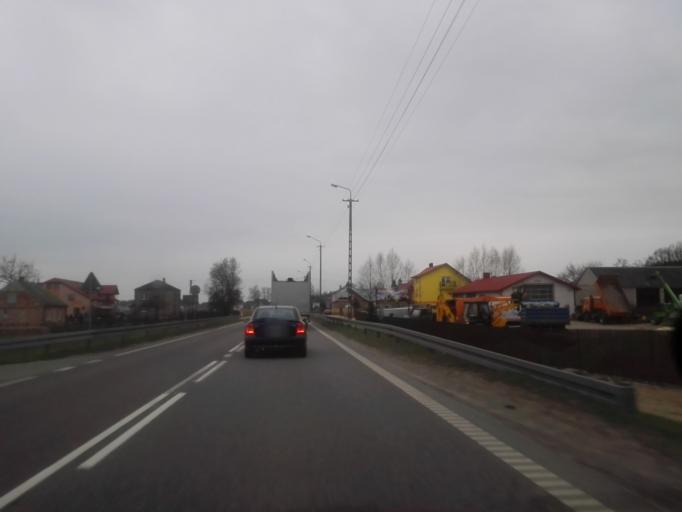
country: PL
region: Podlasie
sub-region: Powiat grajewski
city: Grajewo
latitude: 53.6252
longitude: 22.4062
